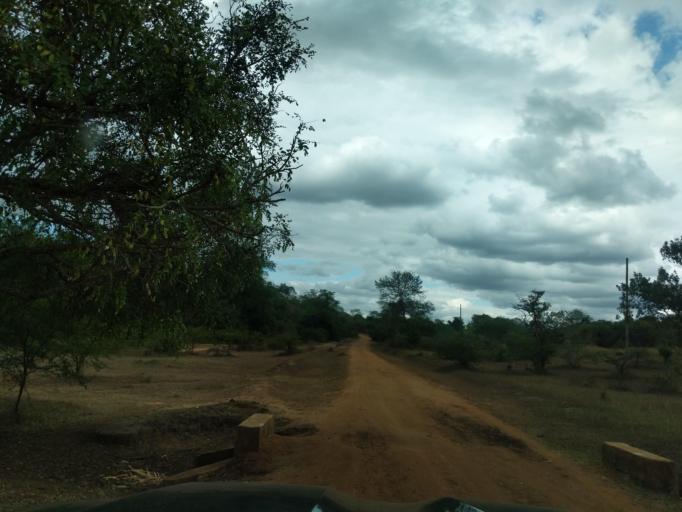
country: TZ
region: Pwani
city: Mvomero
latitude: -5.9375
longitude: 38.4209
